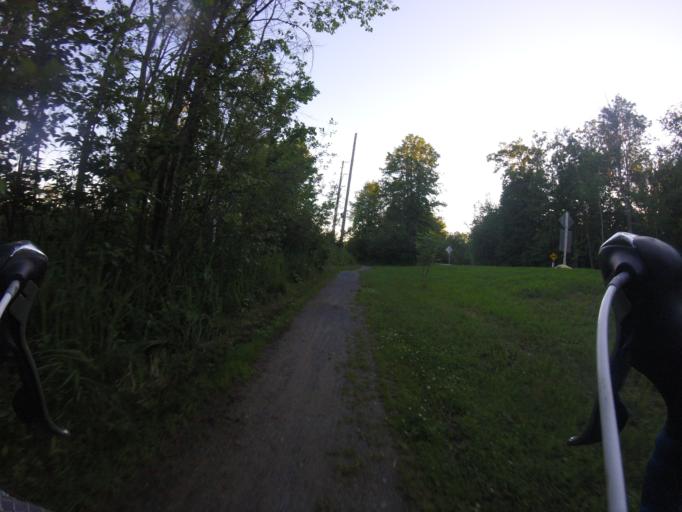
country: CA
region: Ontario
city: Bells Corners
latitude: 45.3463
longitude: -75.8518
